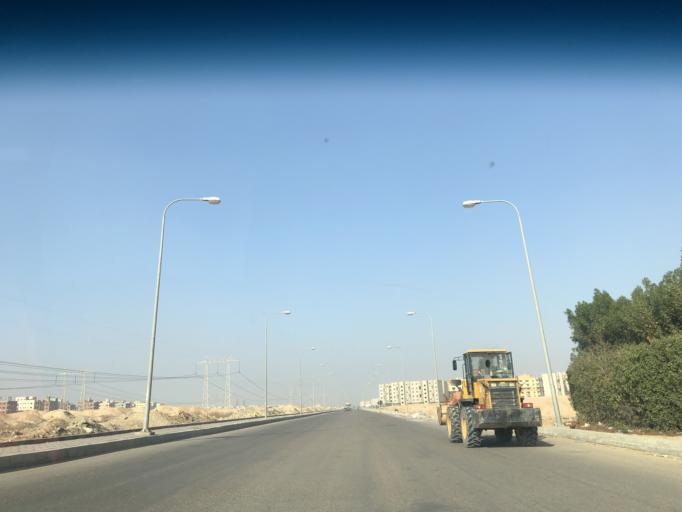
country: EG
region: Al Jizah
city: Madinat Sittah Uktubar
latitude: 29.9152
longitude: 31.0531
